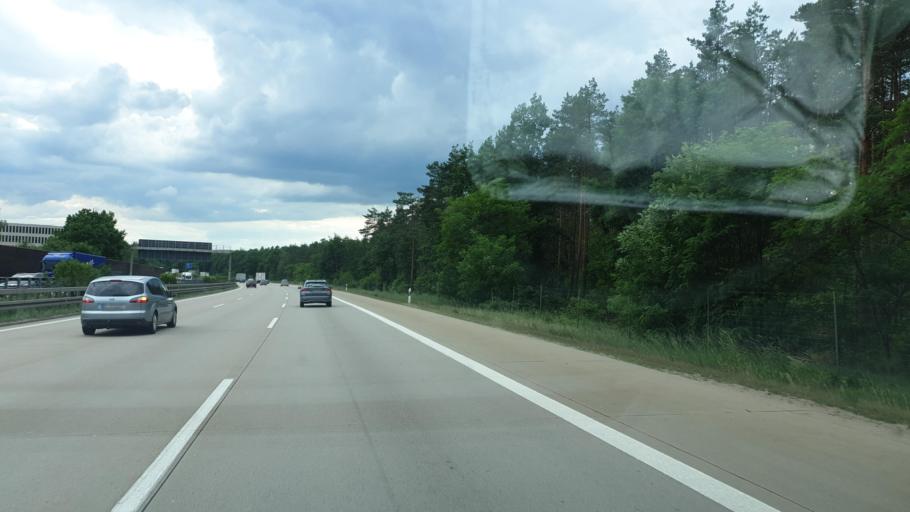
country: DE
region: Saxony
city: Radebeul
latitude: 51.1001
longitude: 13.7075
